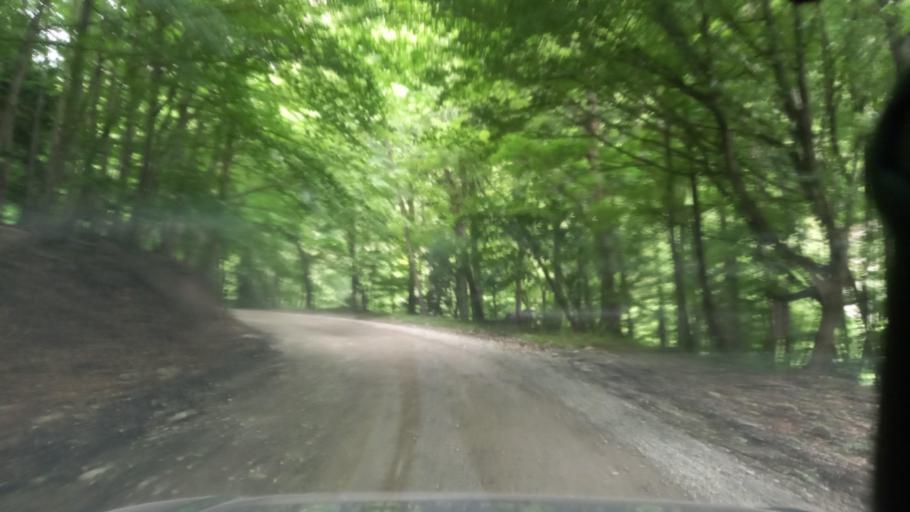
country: RU
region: Karachayevo-Cherkesiya
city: Kurdzhinovo
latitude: 43.8579
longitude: 40.9360
